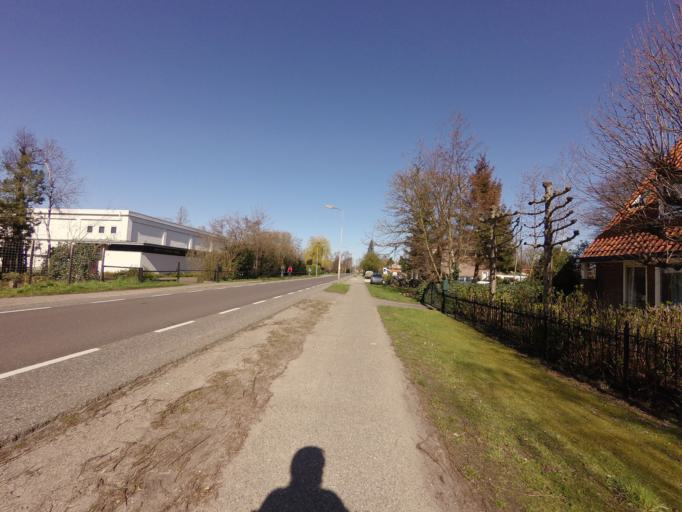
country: NL
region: North Holland
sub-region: Gemeente Wijdemeren
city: Kortenhoef
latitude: 52.2530
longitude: 5.0940
